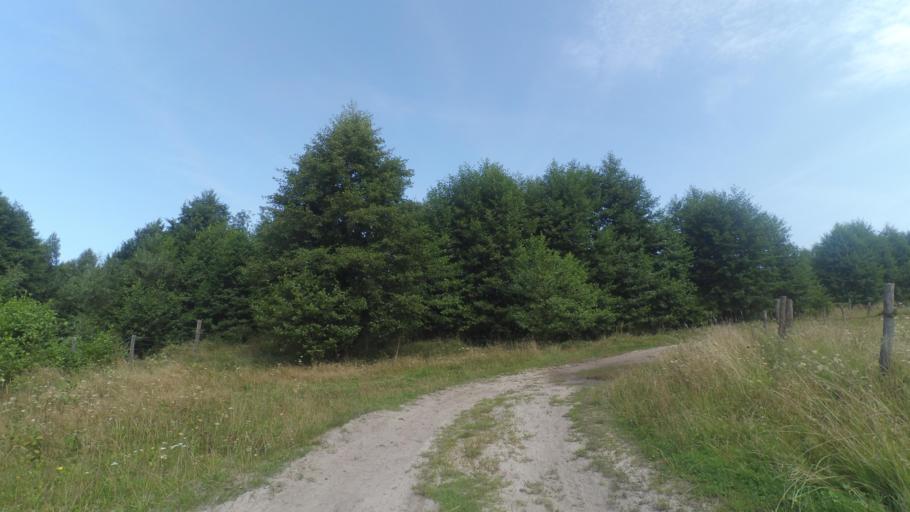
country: PL
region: Lublin Voivodeship
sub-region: Powiat wlodawski
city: Wlodawa
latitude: 51.5004
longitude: 23.6726
